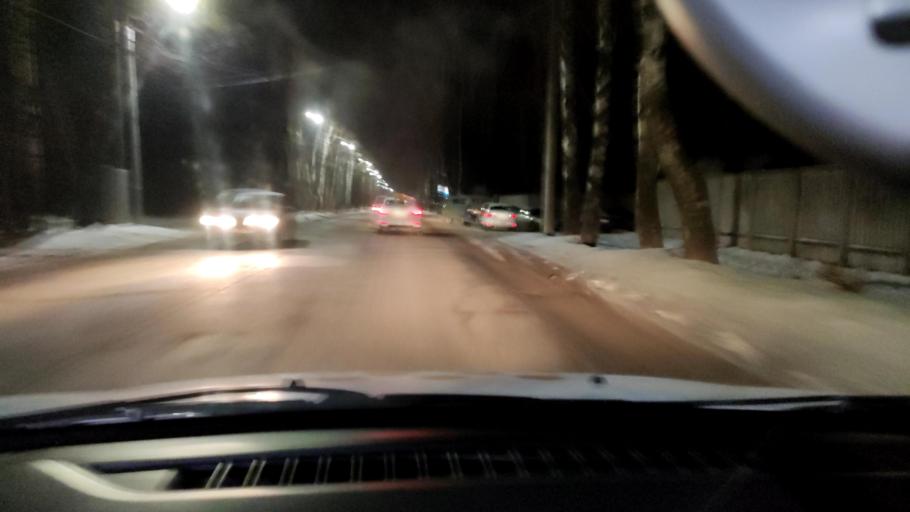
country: RU
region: Perm
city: Kultayevo
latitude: 57.9832
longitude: 55.9199
